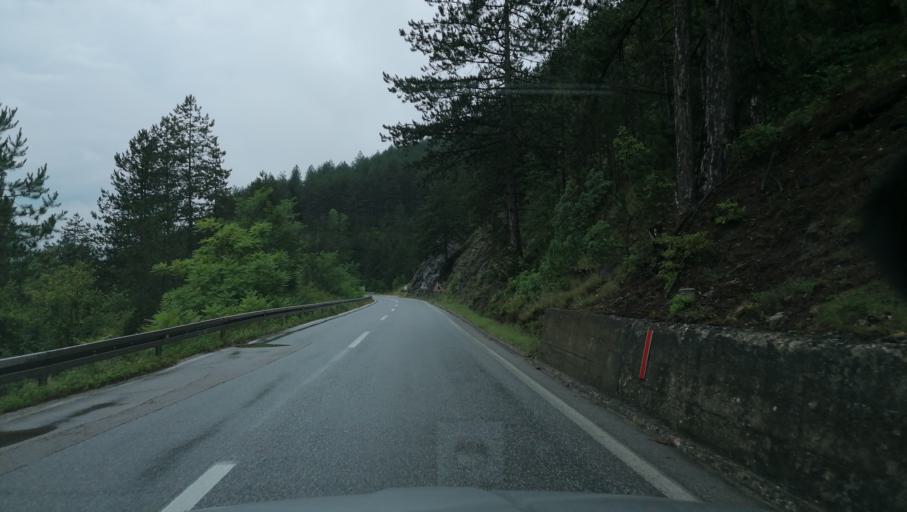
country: BA
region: Republika Srpska
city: Visegrad
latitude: 43.7844
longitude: 19.3201
